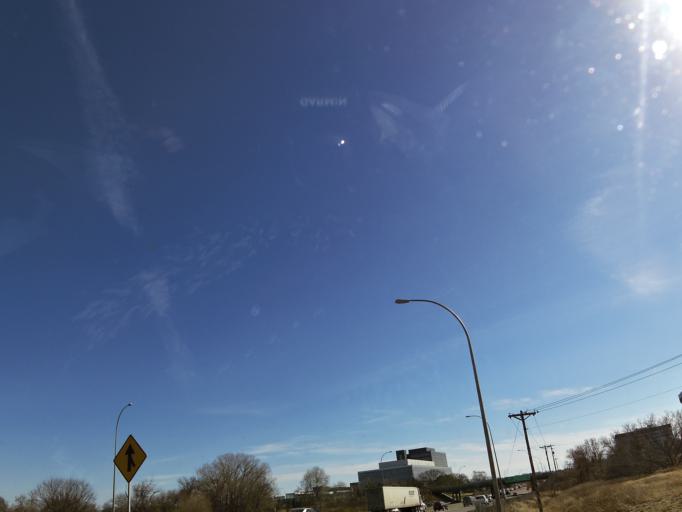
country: US
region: Minnesota
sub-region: Hennepin County
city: Minnetonka Mills
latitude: 44.9811
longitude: -93.4011
